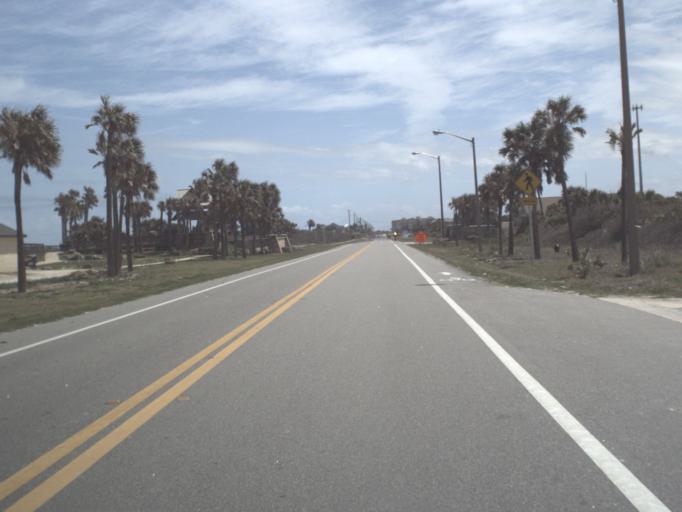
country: US
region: Florida
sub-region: Flagler County
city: Palm Coast
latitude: 29.6658
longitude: -81.2121
